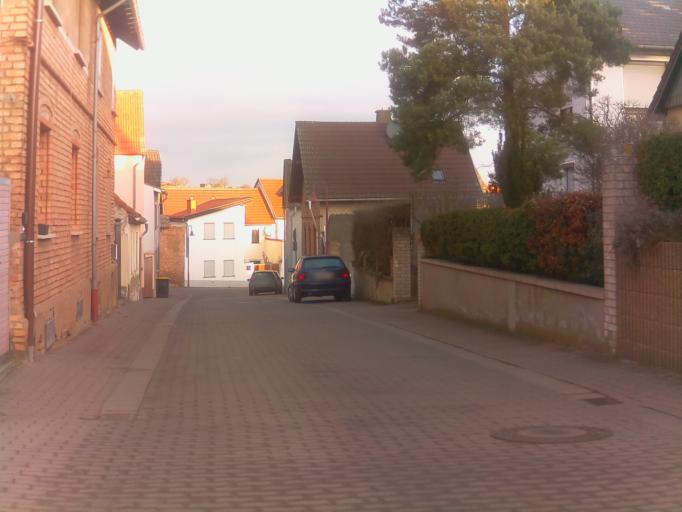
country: DE
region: Rheinland-Pfalz
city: Wendelsheim
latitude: 49.7618
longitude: 7.9841
